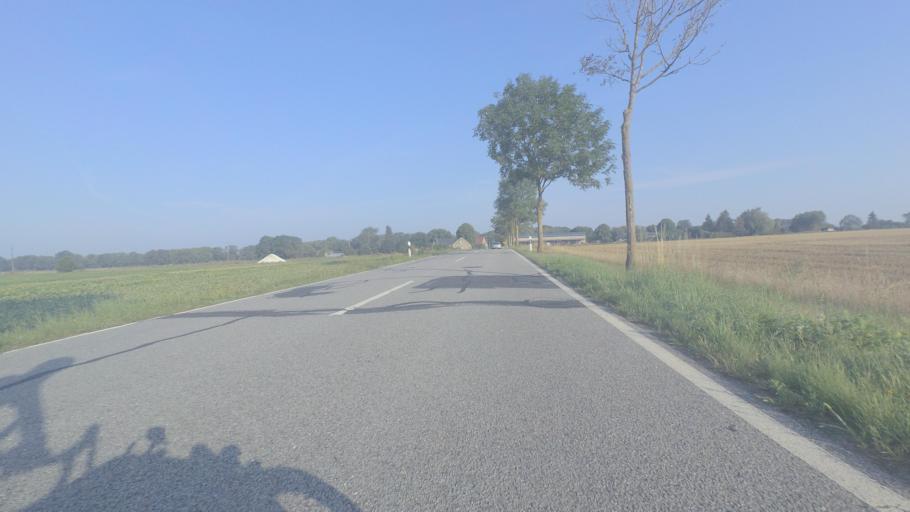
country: DE
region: Mecklenburg-Vorpommern
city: Demmin
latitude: 53.9513
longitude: 13.1149
